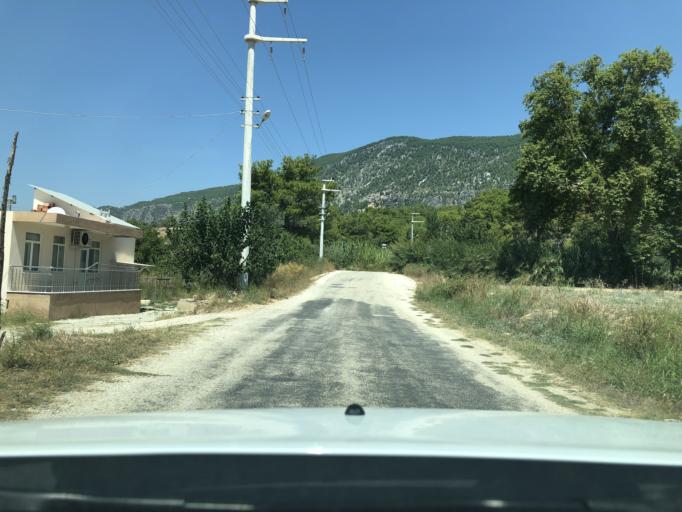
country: TR
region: Antalya
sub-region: Manavgat
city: Kizilagac
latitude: 36.8595
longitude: 31.5634
